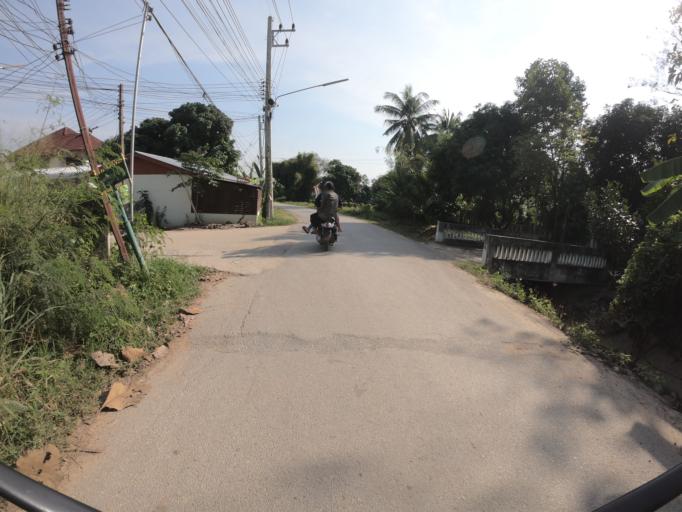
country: TH
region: Chiang Mai
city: Chiang Mai
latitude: 18.8397
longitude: 98.9917
